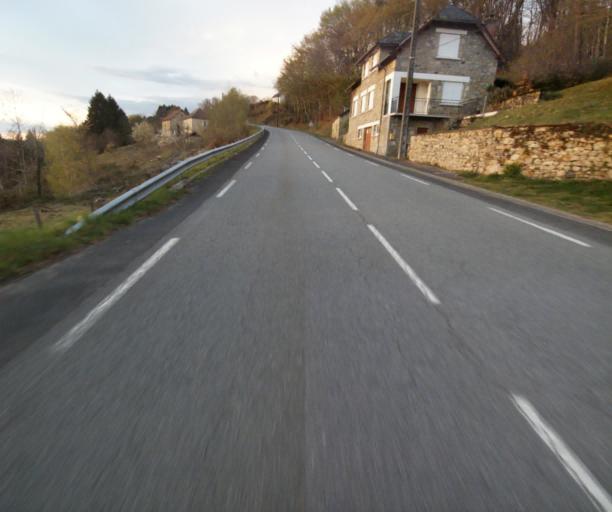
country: FR
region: Limousin
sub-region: Departement de la Correze
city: Laguenne
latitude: 45.2833
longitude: 1.8460
